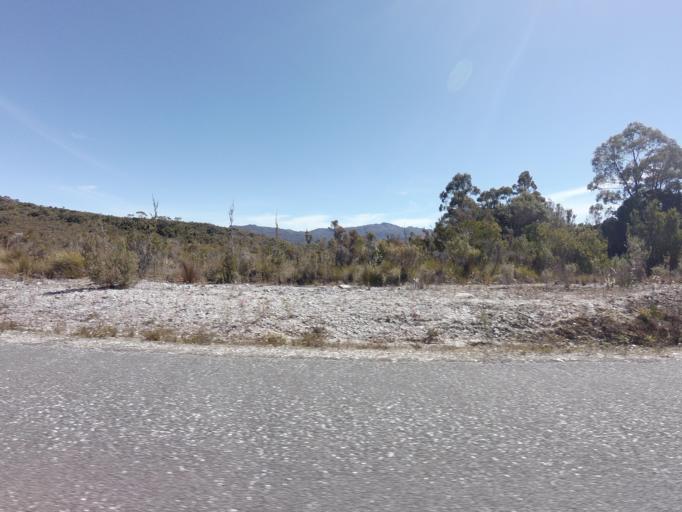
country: AU
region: Tasmania
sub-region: West Coast
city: Queenstown
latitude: -42.7892
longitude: 146.0627
